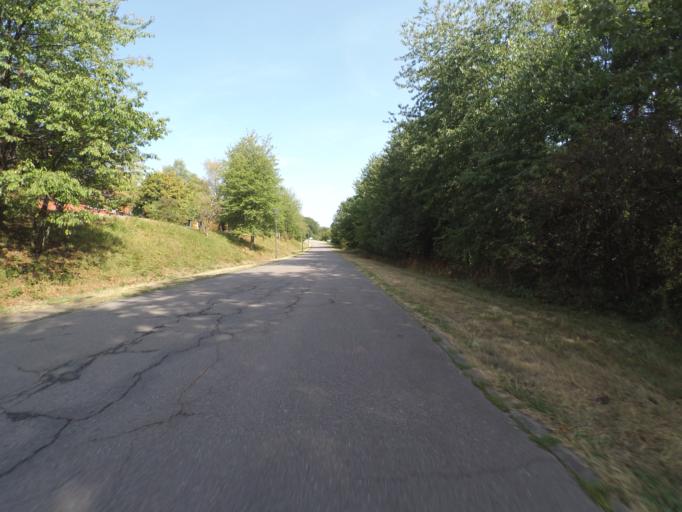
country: DE
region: Rheinland-Pfalz
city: Saarburg
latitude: 49.6166
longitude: 6.5444
